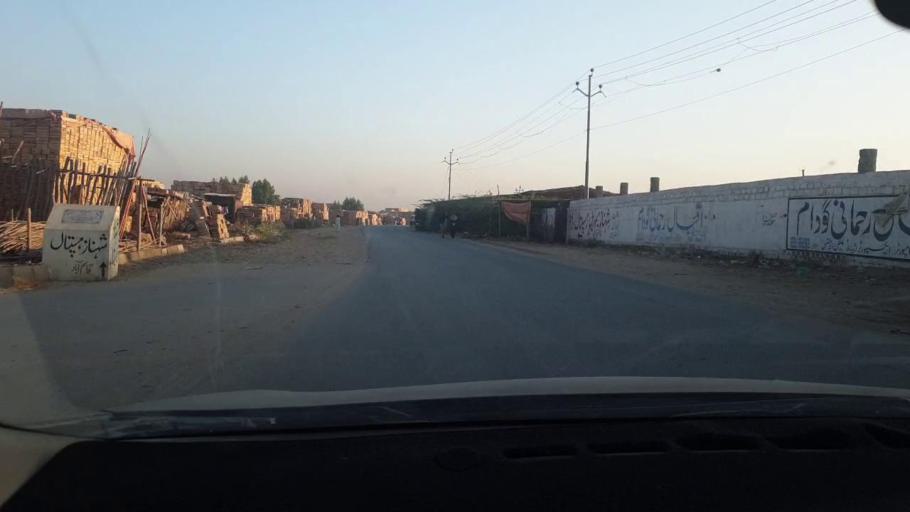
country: PK
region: Sindh
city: Malir Cantonment
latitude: 24.9967
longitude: 67.1431
